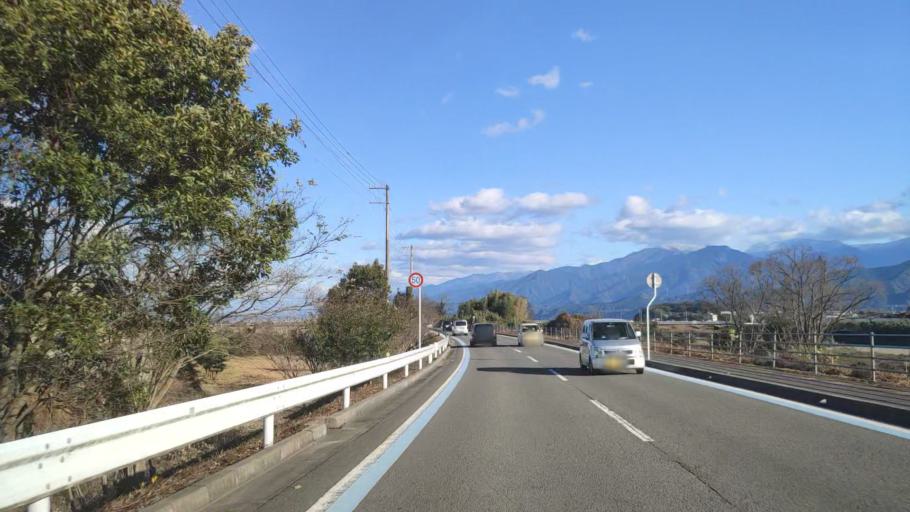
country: JP
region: Ehime
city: Saijo
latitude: 33.9066
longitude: 133.1137
